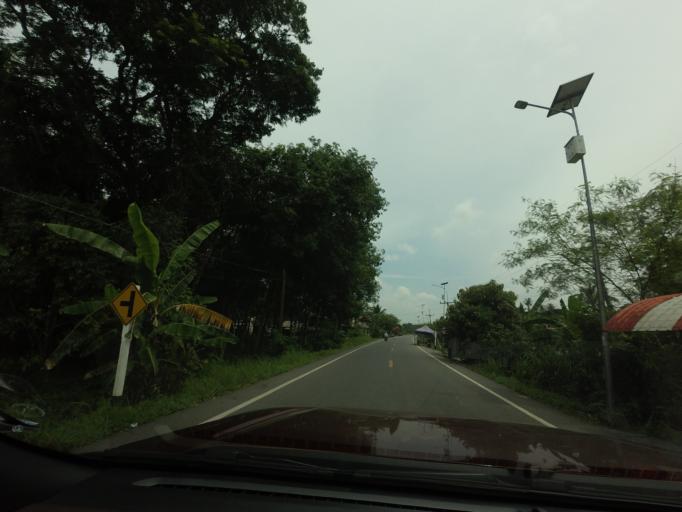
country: TH
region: Pattani
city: Yarang
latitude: 6.7127
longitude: 101.3049
